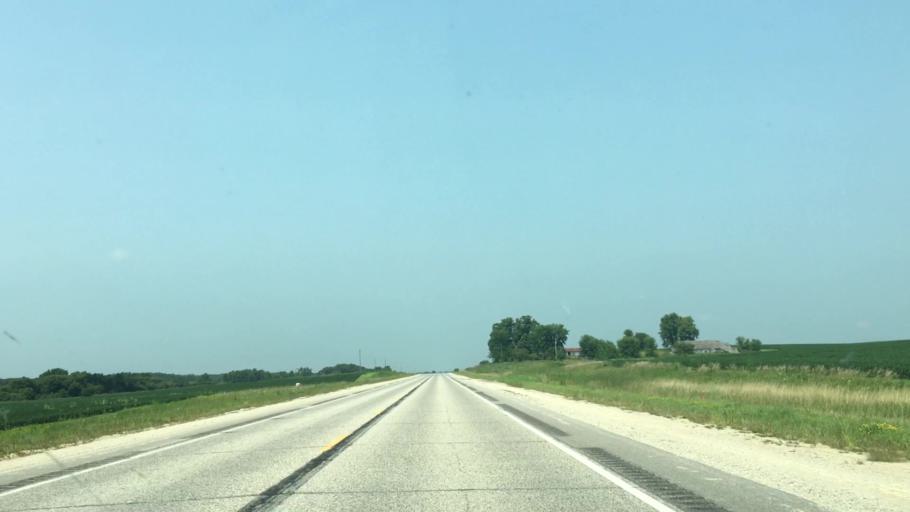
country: US
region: Iowa
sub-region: Fayette County
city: Fayette
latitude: 42.7928
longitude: -91.8049
